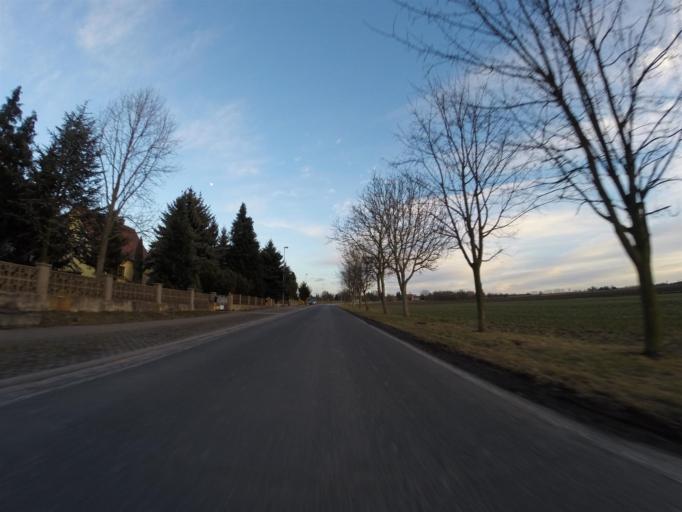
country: DE
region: Thuringia
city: Lehesten
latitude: 51.0092
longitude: 11.5563
